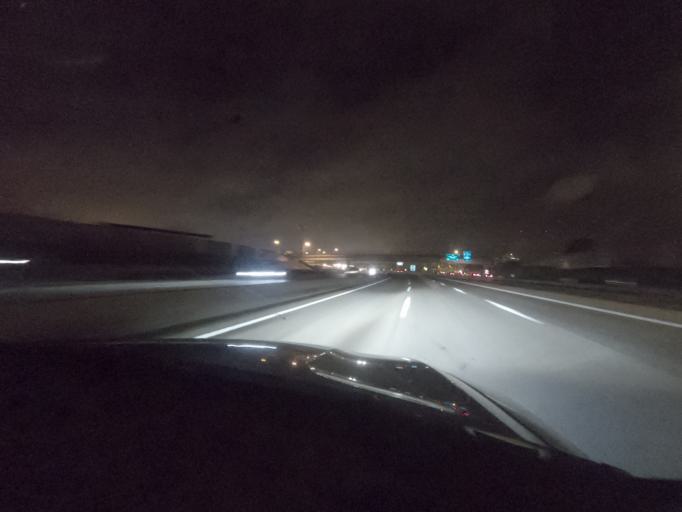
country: PT
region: Lisbon
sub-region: Alenquer
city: Carregado
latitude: 39.0222
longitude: -8.9647
